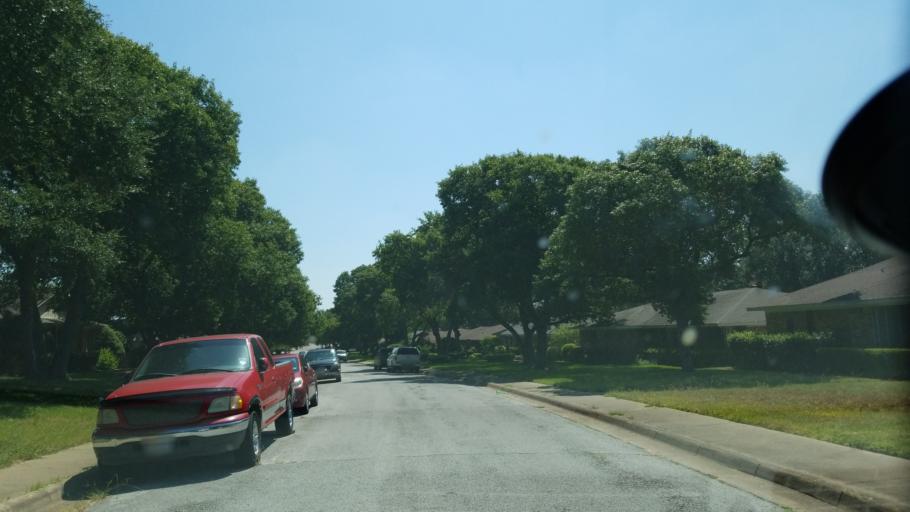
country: US
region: Texas
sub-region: Dallas County
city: Duncanville
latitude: 32.6550
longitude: -96.8942
